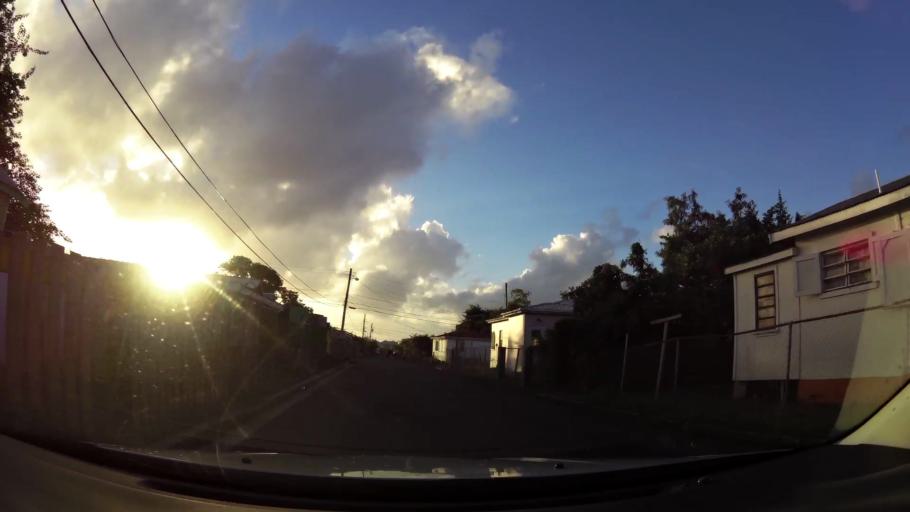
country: AG
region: Saint John
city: Saint John's
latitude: 17.1303
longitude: -61.8475
